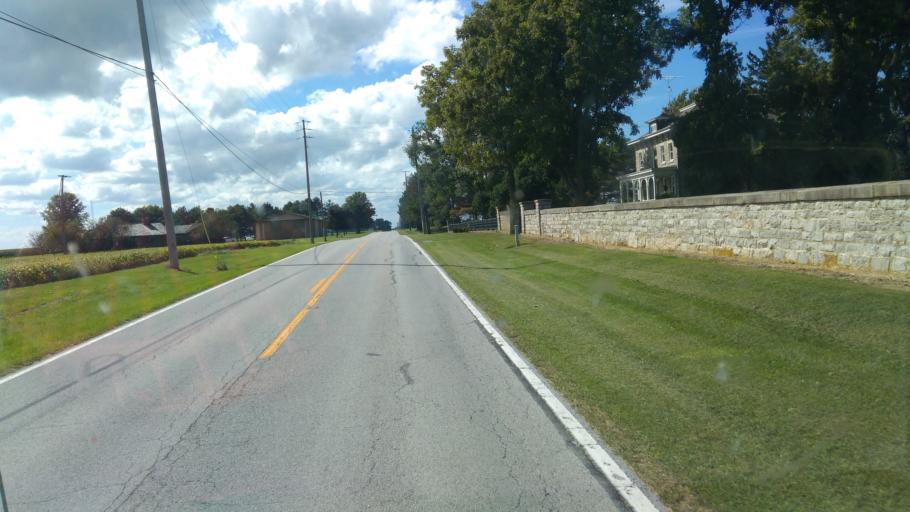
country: US
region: Ohio
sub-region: Sandusky County
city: Clyde
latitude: 41.3867
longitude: -82.8909
